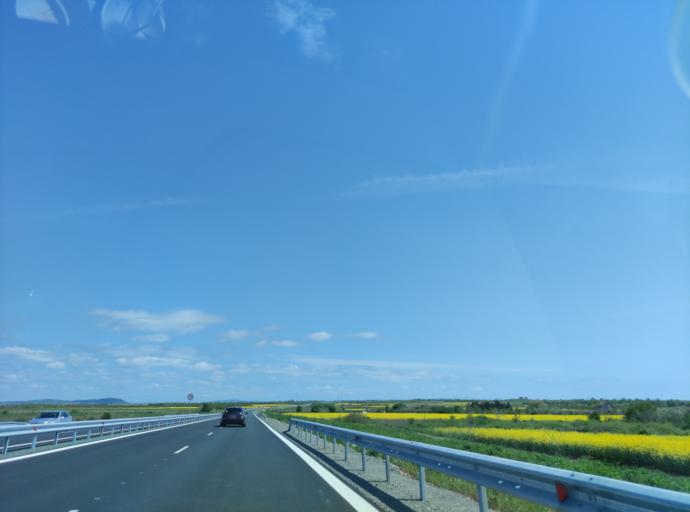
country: BG
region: Burgas
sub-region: Obshtina Pomorie
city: Pomorie
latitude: 42.5674
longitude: 27.5727
